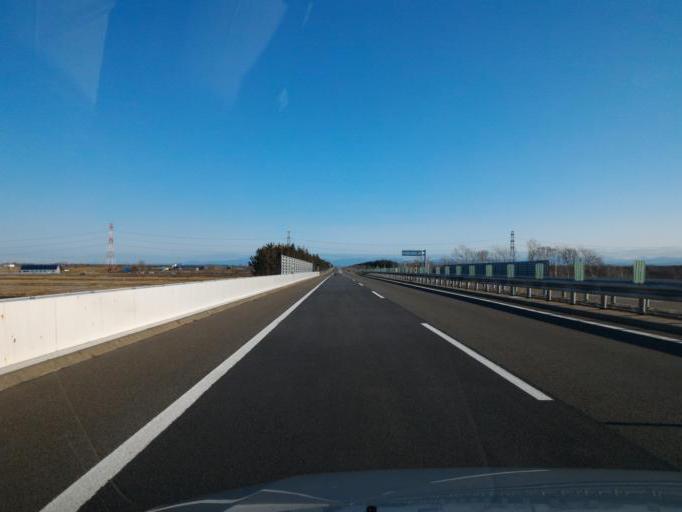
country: JP
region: Hokkaido
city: Ebetsu
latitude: 43.1164
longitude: 141.6219
